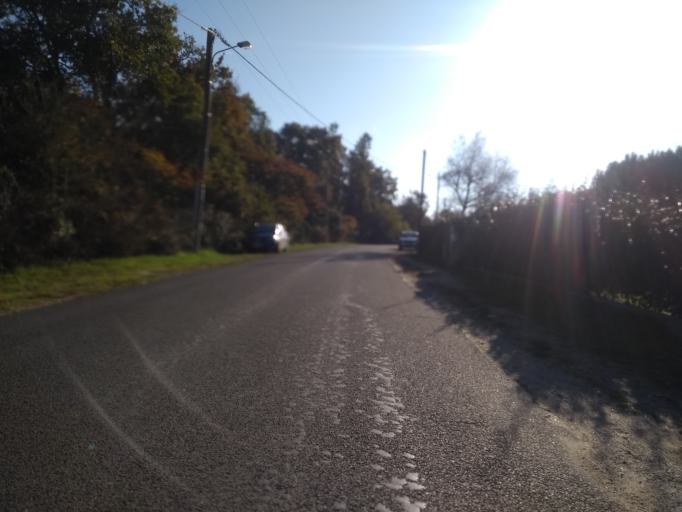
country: FR
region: Aquitaine
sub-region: Departement de la Gironde
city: Ayguemorte-les-Graves
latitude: 44.7204
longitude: -0.5009
